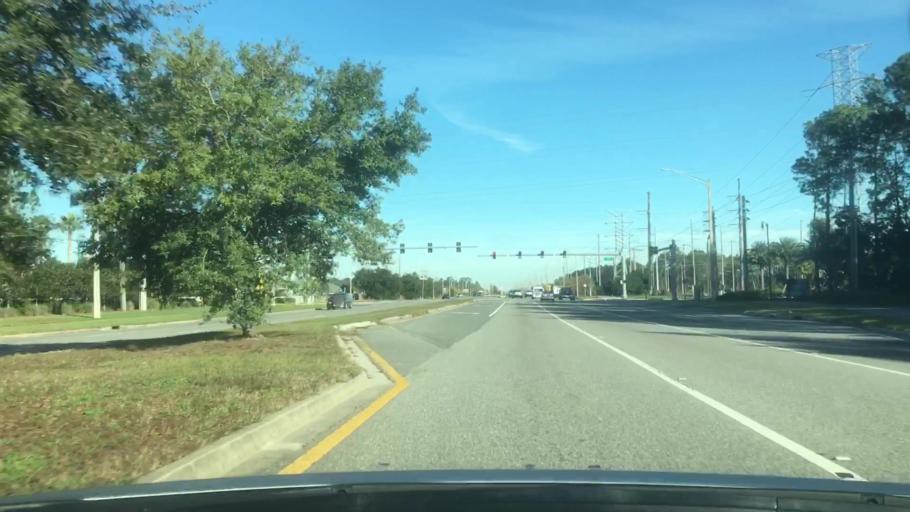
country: US
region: Florida
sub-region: Duval County
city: Neptune Beach
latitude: 30.2941
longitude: -81.4888
